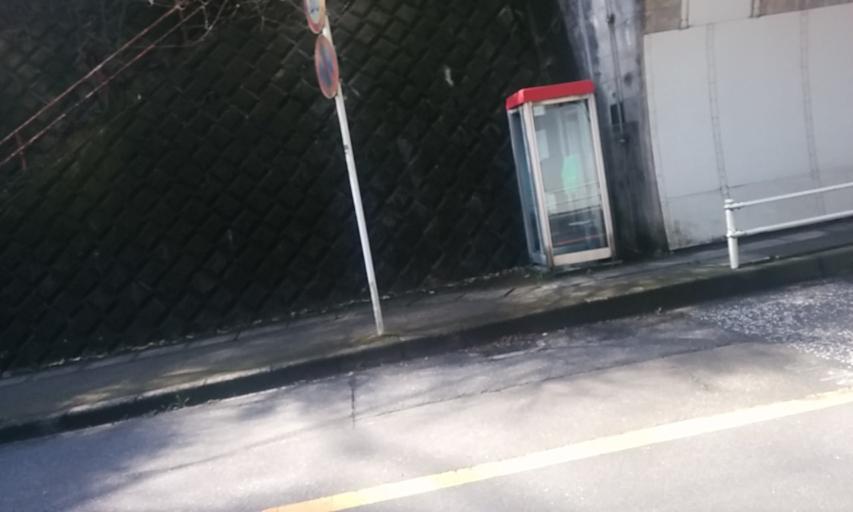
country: JP
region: Kanagawa
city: Kamakura
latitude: 35.3211
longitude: 139.5403
